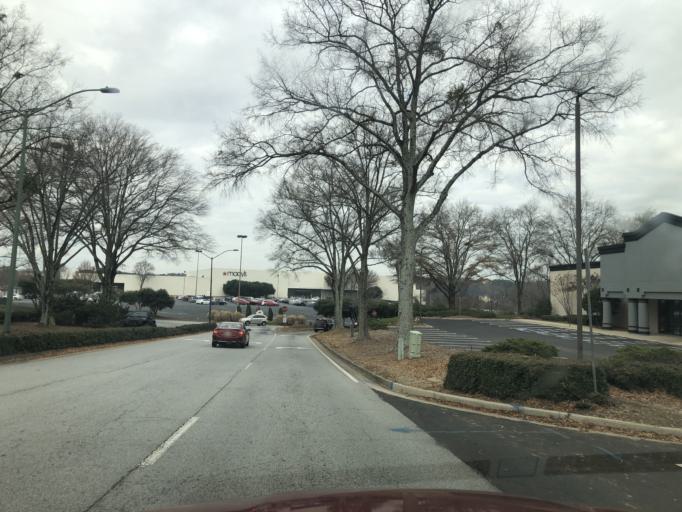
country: US
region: Georgia
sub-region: Clayton County
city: Morrow
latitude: 33.5758
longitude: -84.3472
